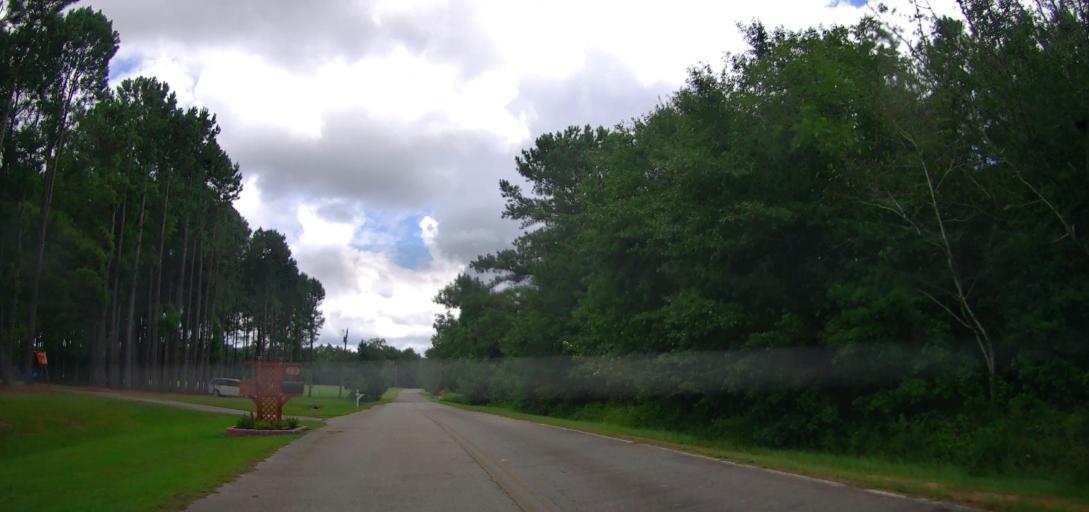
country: US
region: Georgia
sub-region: Pulaski County
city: Hawkinsville
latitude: 32.3156
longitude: -83.5328
